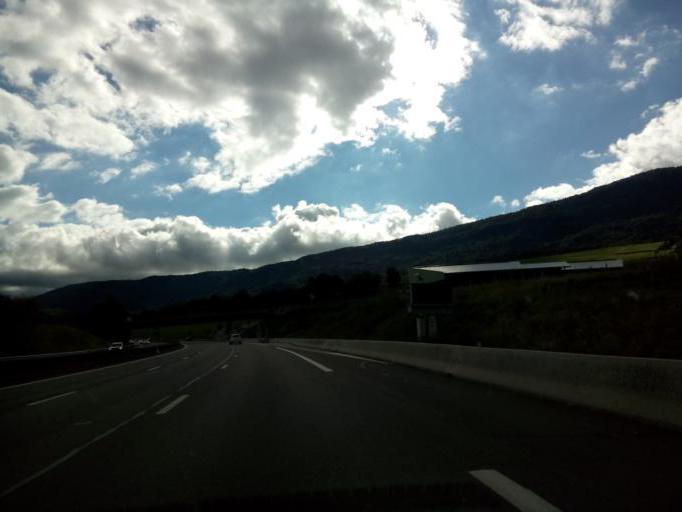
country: FR
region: Rhone-Alpes
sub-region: Departement de la Savoie
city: La Motte-Servolex
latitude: 45.6029
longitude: 5.8586
